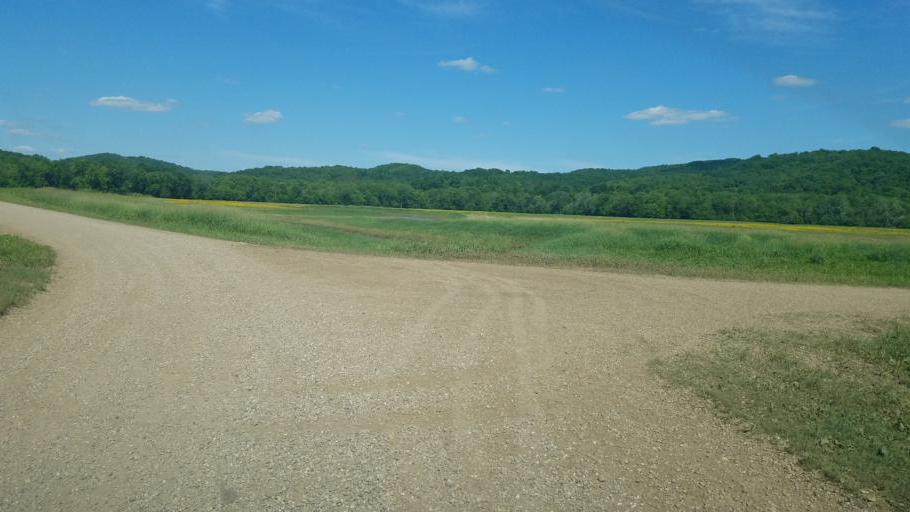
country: US
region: Ohio
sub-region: Tuscarawas County
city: Newcomerstown
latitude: 40.2066
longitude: -81.6788
